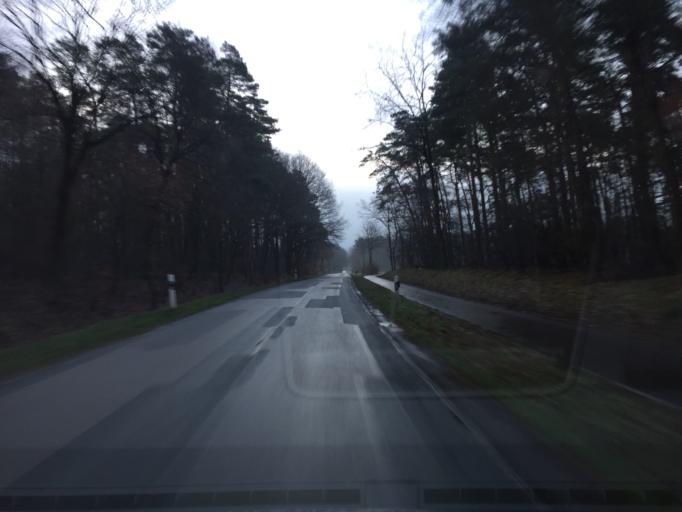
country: DE
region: Lower Saxony
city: Liebenau
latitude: 52.6175
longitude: 9.0713
